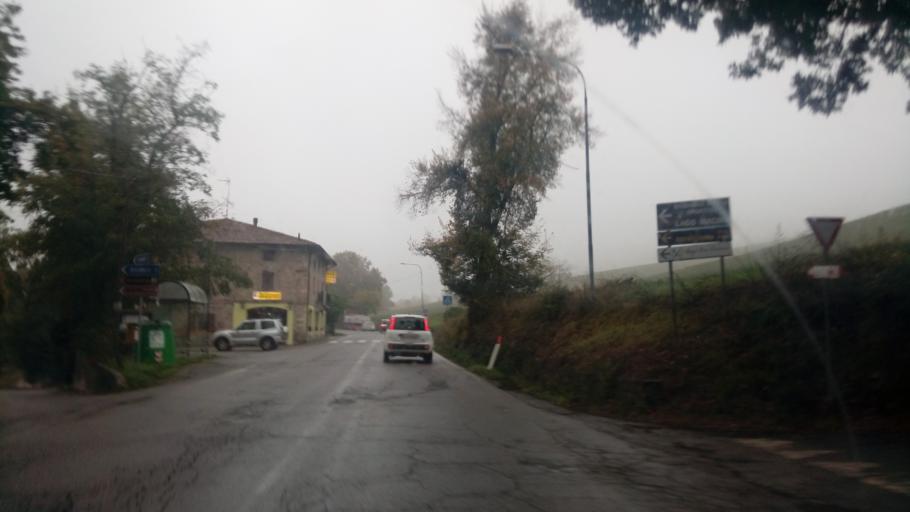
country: IT
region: Emilia-Romagna
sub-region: Provincia di Reggio Emilia
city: Viano
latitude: 44.5458
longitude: 10.6484
